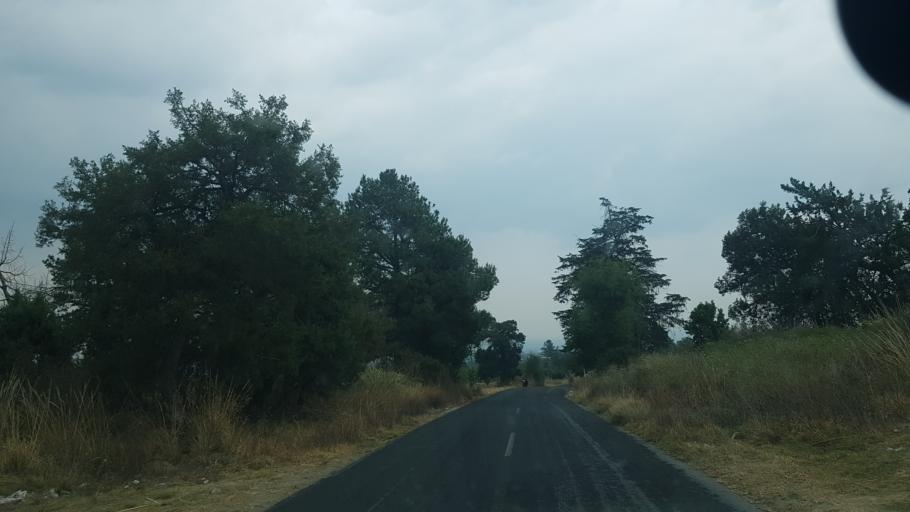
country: MX
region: Puebla
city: San Lorenzo Chiautzingo
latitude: 19.1920
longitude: -98.4724
